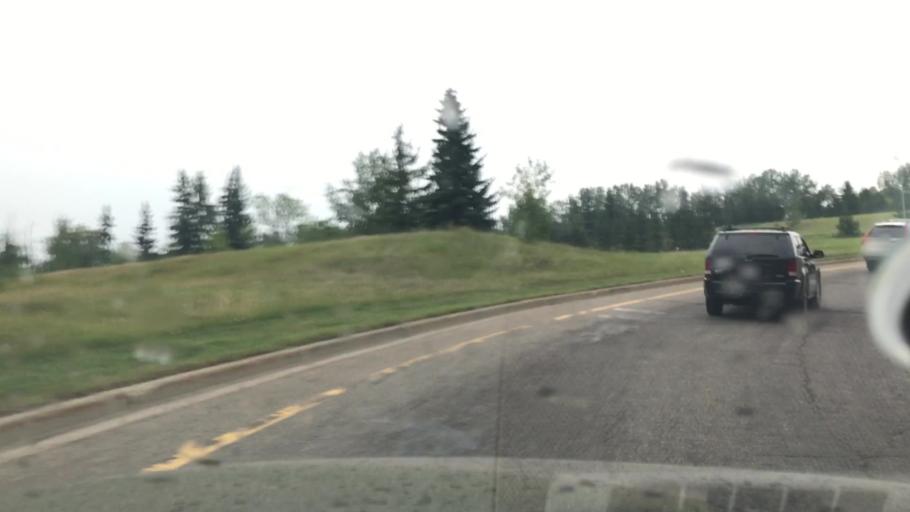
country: CA
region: Alberta
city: Edmonton
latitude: 53.4839
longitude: -113.5720
